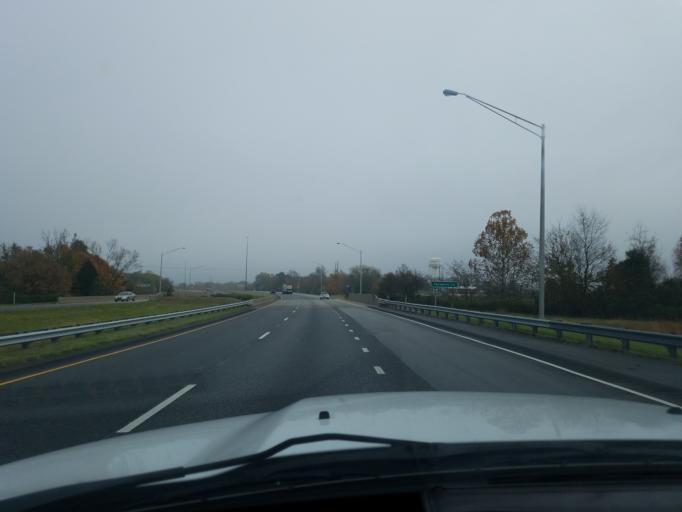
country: US
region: Indiana
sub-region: Floyd County
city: Georgetown
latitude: 38.2829
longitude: -85.9193
